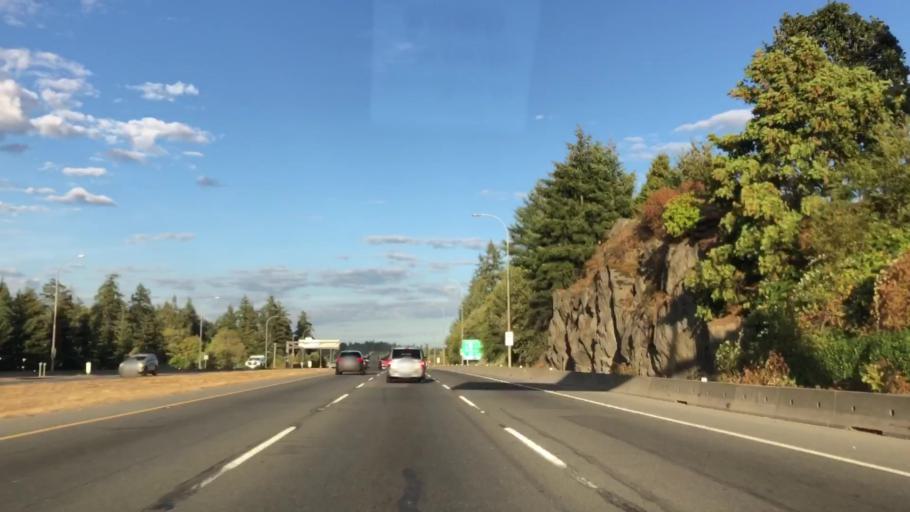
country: CA
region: British Columbia
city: Colwood
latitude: 48.4623
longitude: -123.4440
